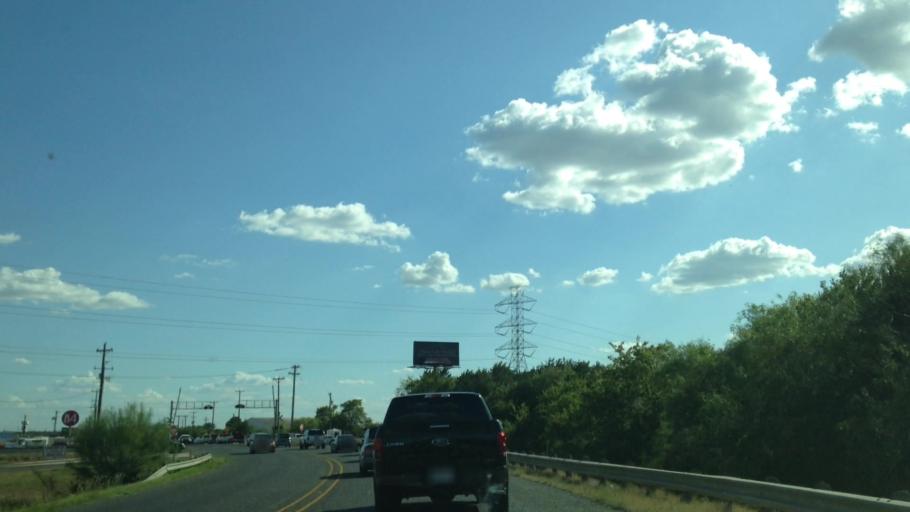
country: US
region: Texas
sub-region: Comal County
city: Garden Ridge
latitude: 29.6101
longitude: -98.3250
